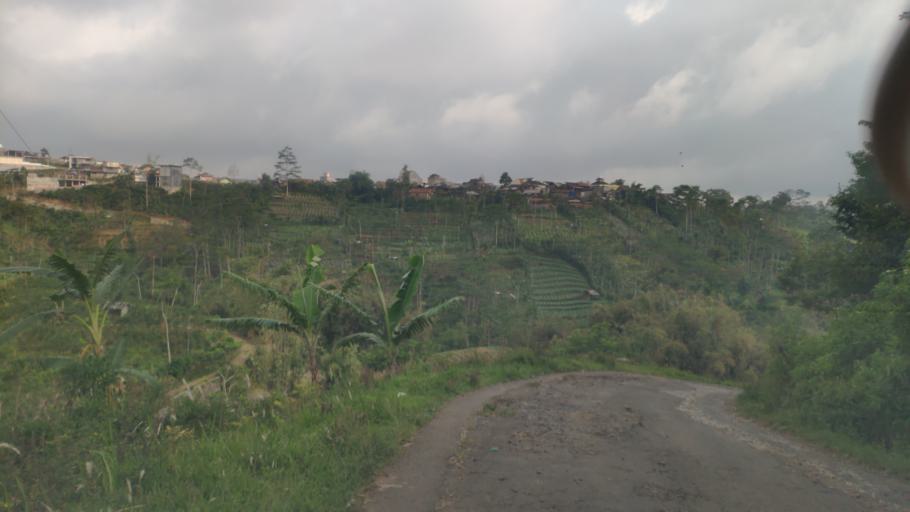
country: ID
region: Central Java
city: Wonosobo
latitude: -7.2789
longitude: 109.8315
